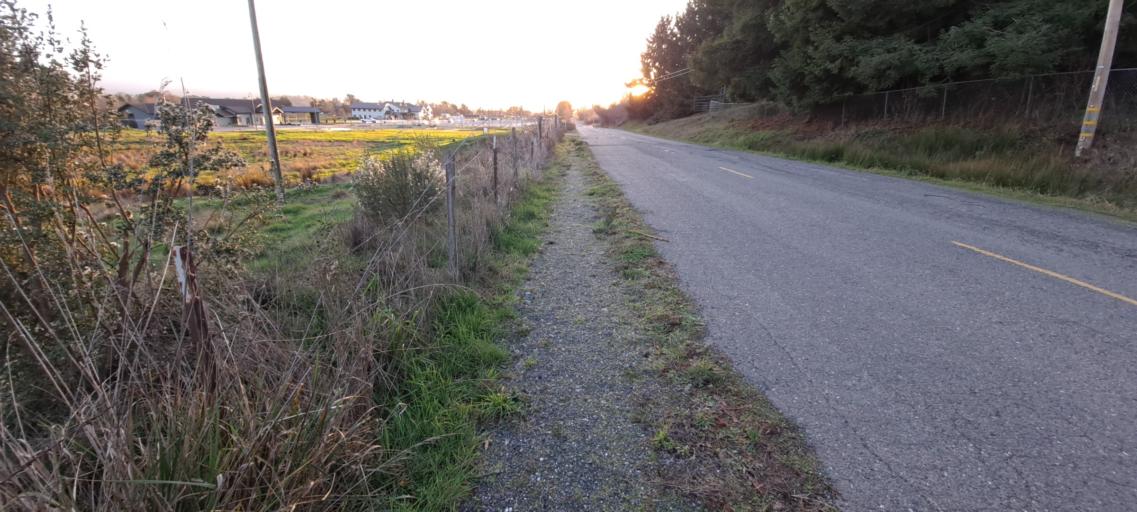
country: US
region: California
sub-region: Humboldt County
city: Fortuna
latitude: 40.5960
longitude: -124.1316
